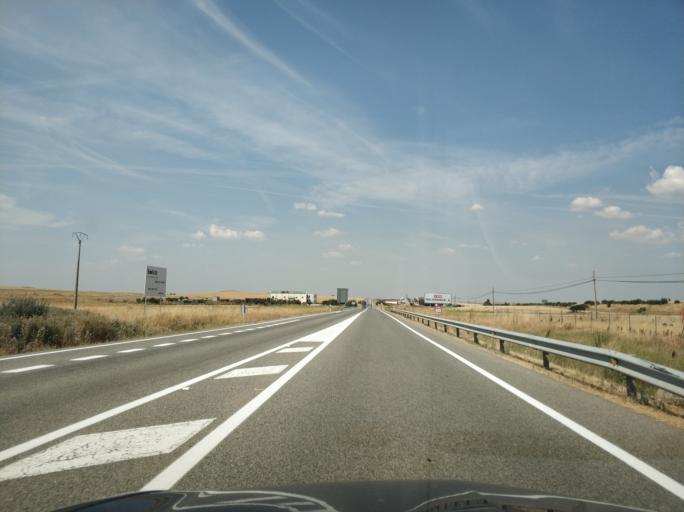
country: ES
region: Castille and Leon
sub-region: Provincia de Salamanca
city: Arapiles
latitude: 40.8977
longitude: -5.6644
